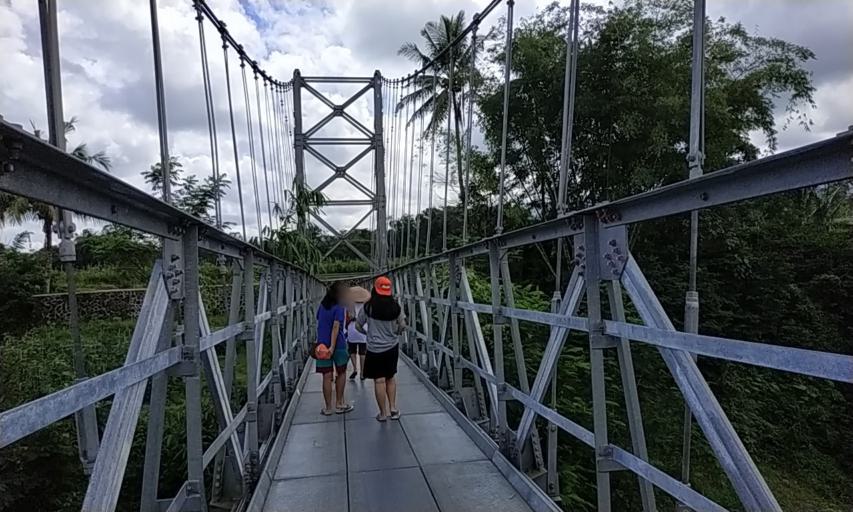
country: ID
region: Central Java
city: Muntilan
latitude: -7.5370
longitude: 110.3570
